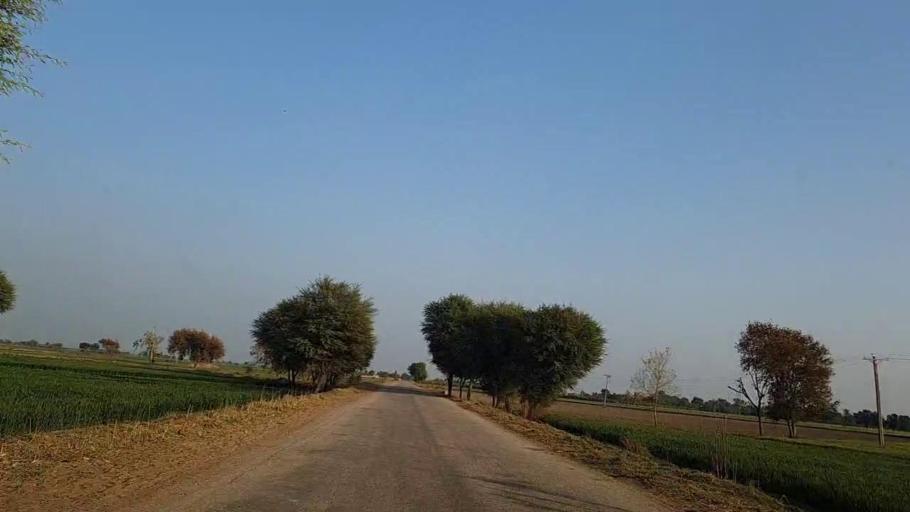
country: PK
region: Sindh
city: Sakrand
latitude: 26.0429
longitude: 68.4245
